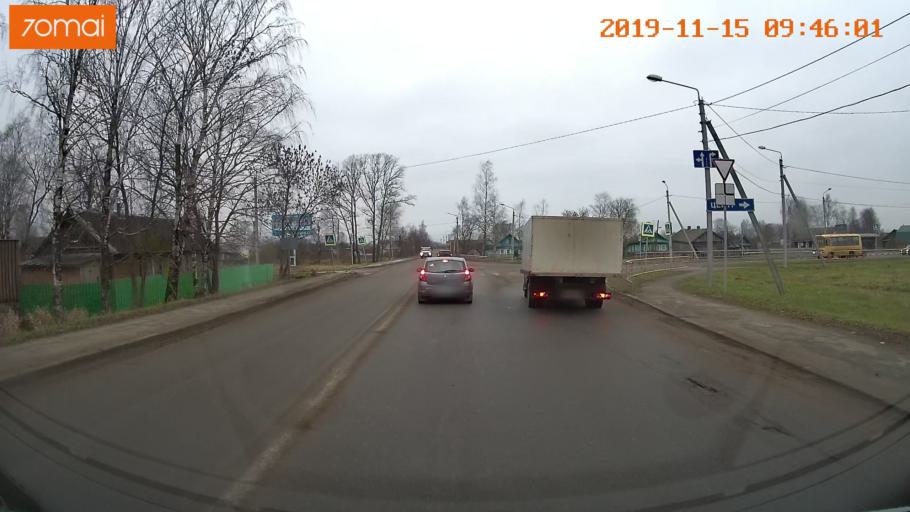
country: RU
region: Vologda
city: Sheksna
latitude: 59.2114
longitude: 38.5120
